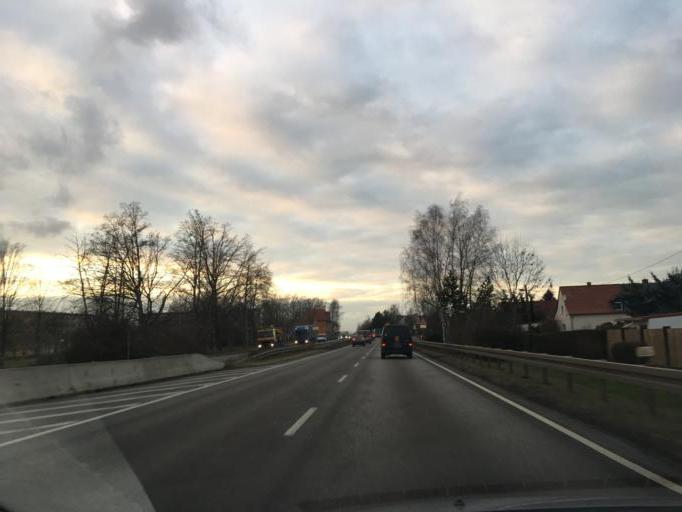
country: DE
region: Saxony
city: Espenhain
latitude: 51.1910
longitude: 12.4706
